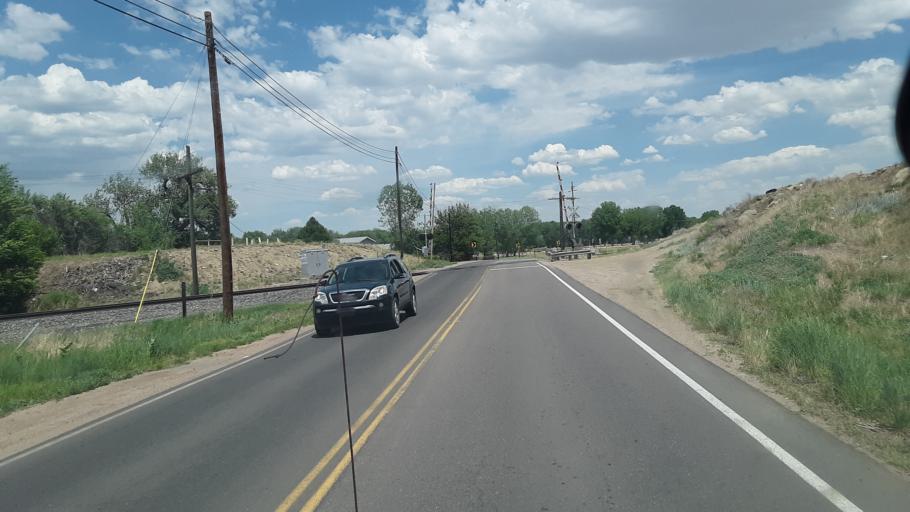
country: US
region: Colorado
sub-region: Fremont County
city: Florence
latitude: 38.4055
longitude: -105.1494
